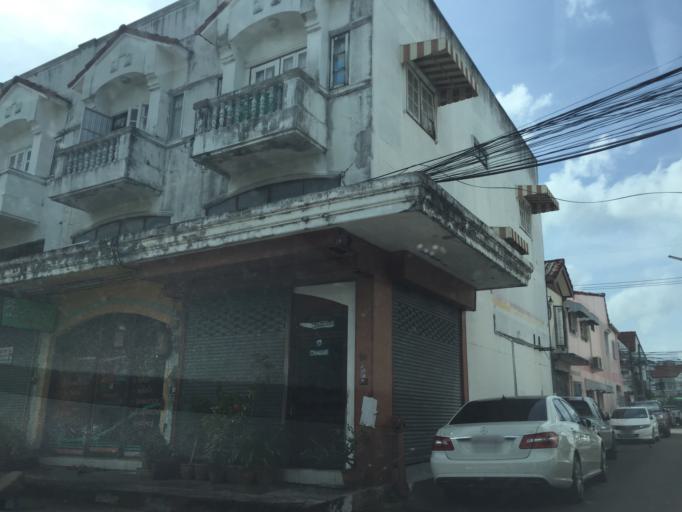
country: TH
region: Phuket
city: Wichit
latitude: 7.9058
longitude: 98.3769
